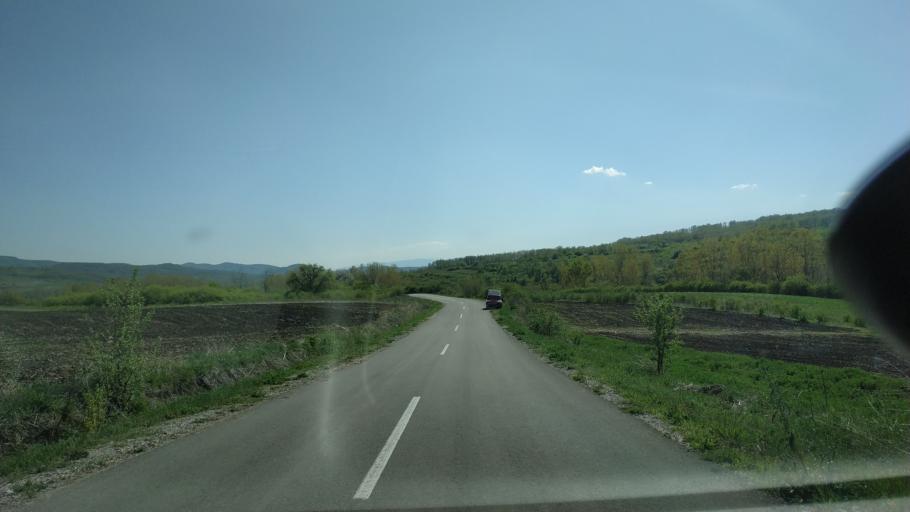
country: RS
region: Central Serbia
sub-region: Zajecarski Okrug
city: Soko Banja
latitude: 43.4872
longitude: 21.8683
